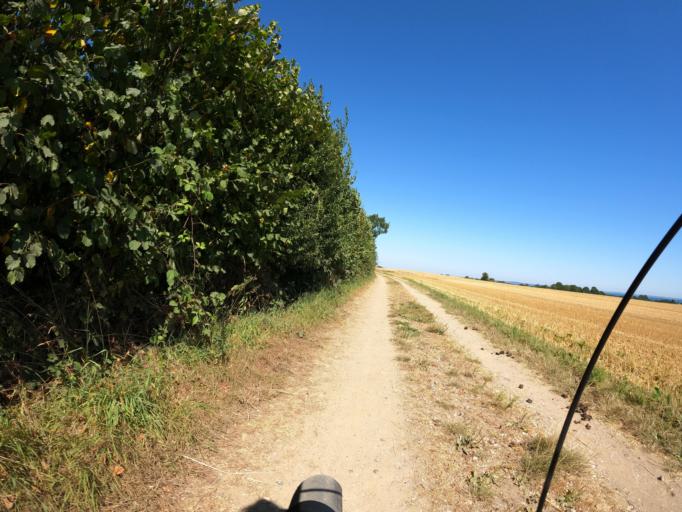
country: DE
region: Schleswig-Holstein
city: Steinbergkirche
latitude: 54.7865
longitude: 9.7547
